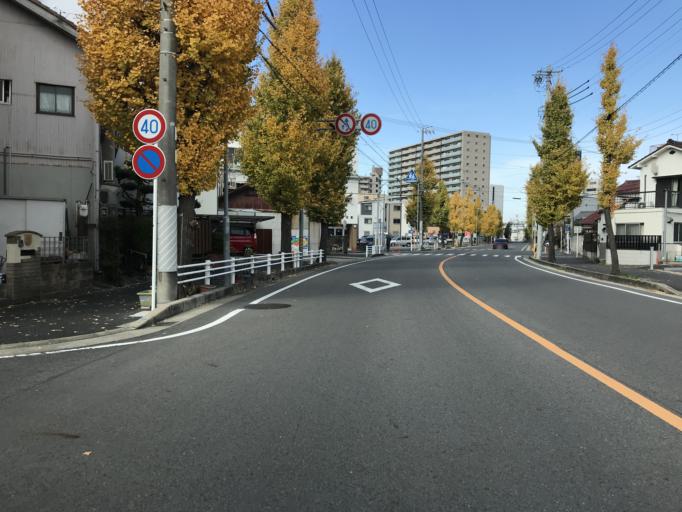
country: JP
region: Aichi
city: Nagoya-shi
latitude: 35.1946
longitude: 136.9233
